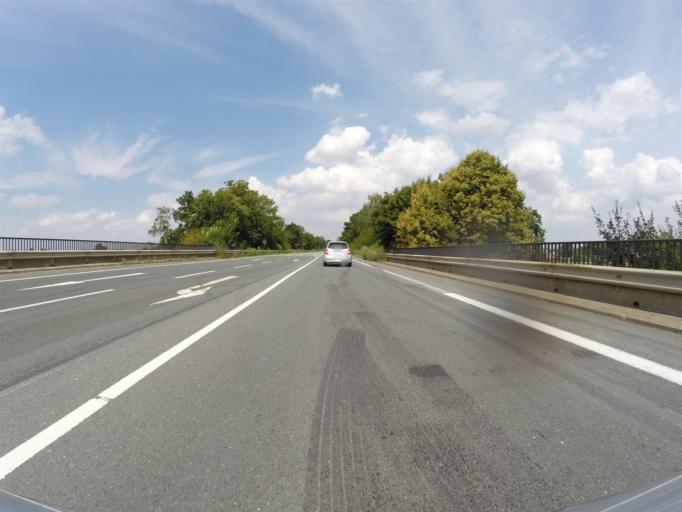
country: DE
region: North Rhine-Westphalia
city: Buende
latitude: 52.2038
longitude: 8.5449
